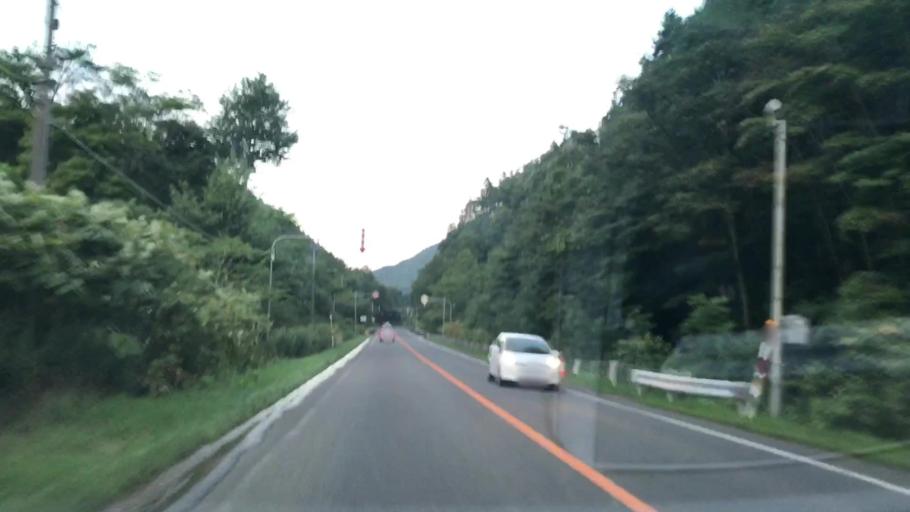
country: JP
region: Hokkaido
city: Sapporo
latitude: 42.9435
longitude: 141.1310
